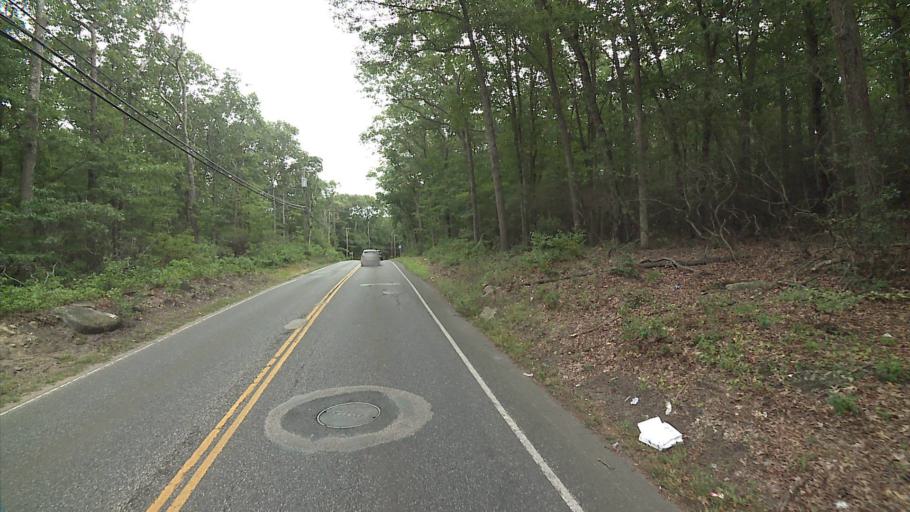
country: US
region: Connecticut
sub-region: New London County
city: Niantic
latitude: 41.3195
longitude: -72.2194
